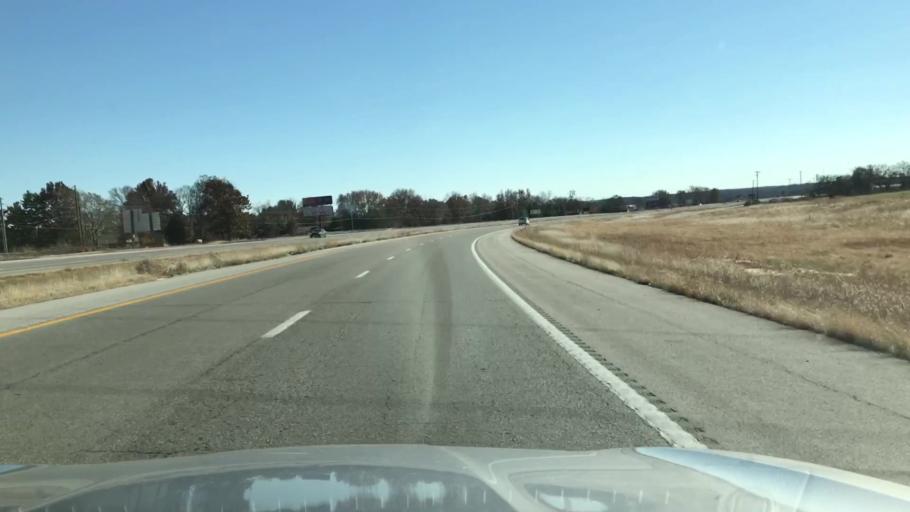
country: US
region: Missouri
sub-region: Jasper County
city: Carthage
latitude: 37.1312
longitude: -94.3121
